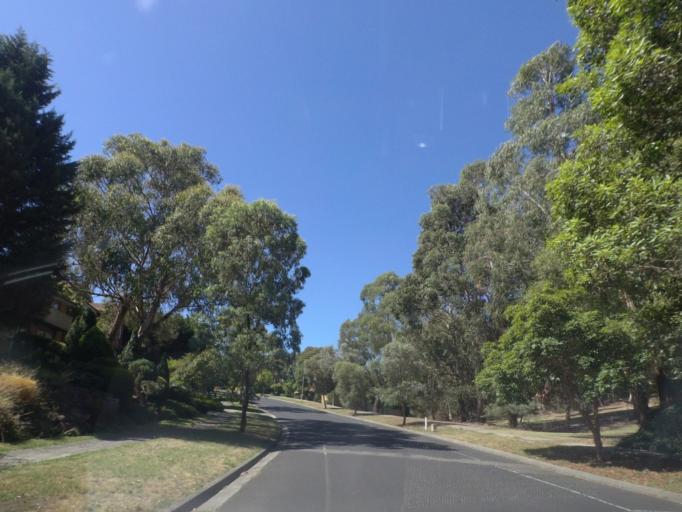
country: AU
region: Victoria
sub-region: Manningham
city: Park Orchards
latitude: -37.7956
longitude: 145.2241
